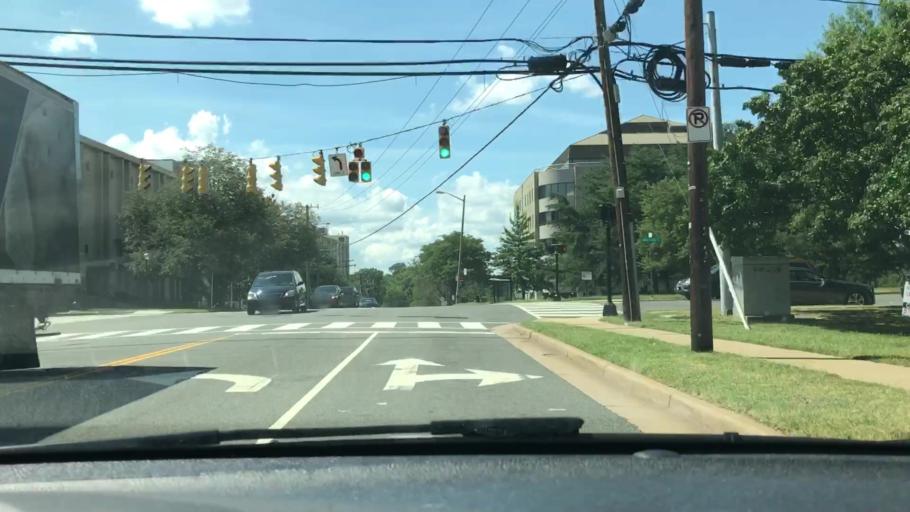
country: US
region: Virginia
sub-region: Fairfax County
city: Lincolnia
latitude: 38.8130
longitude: -77.1369
